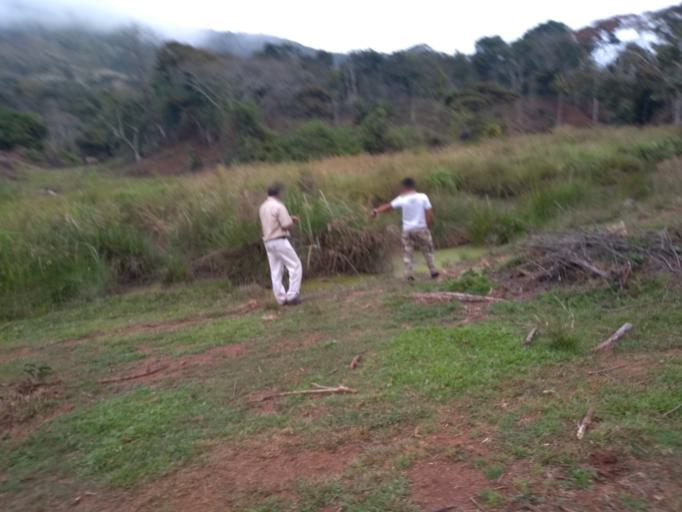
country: CO
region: Cesar
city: Manaure Balcon del Cesar
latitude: 10.1685
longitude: -73.0222
